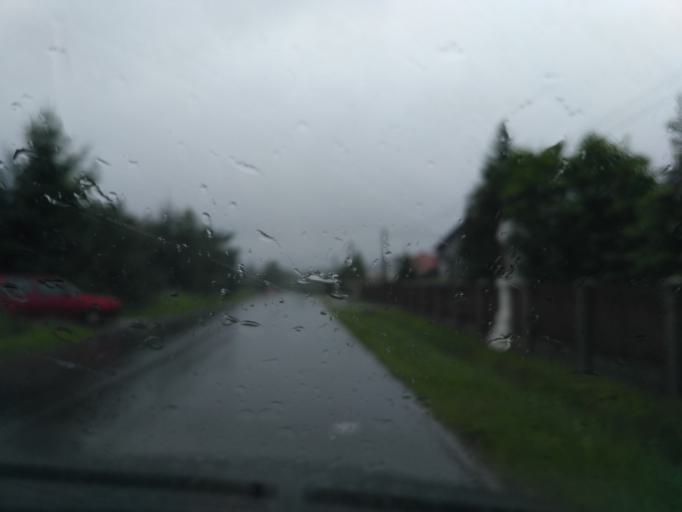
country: PL
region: Subcarpathian Voivodeship
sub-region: Powiat jasielski
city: Debowiec
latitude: 49.6743
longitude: 21.4556
